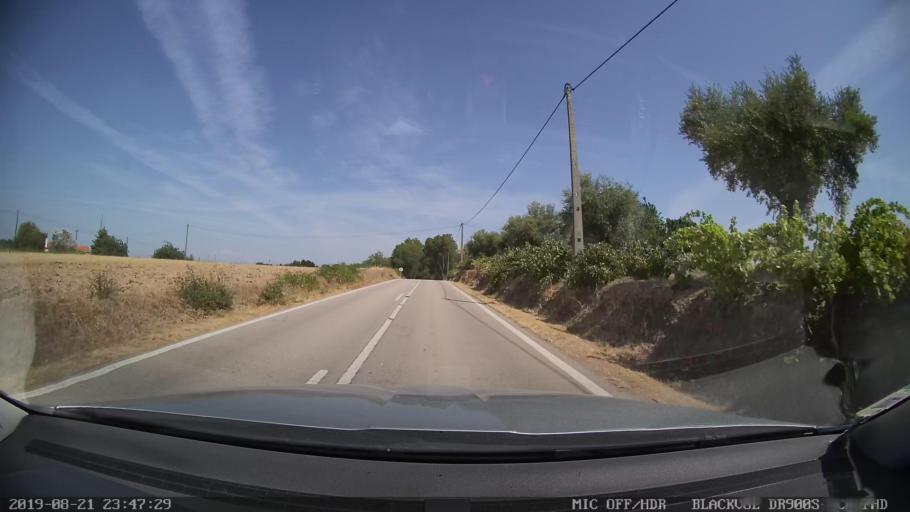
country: PT
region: Castelo Branco
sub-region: Idanha-A-Nova
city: Idanha-a-Nova
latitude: 39.8525
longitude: -7.2574
